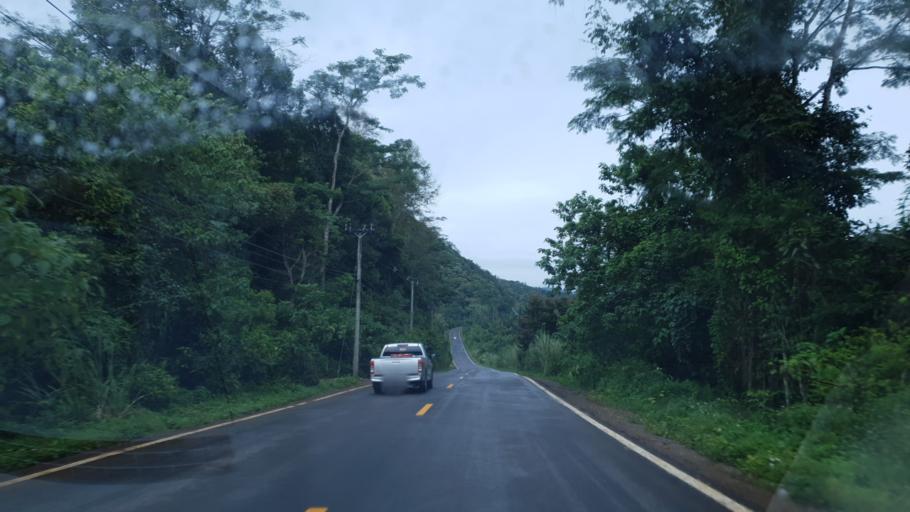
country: TH
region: Mae Hong Son
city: Ban Huai I Huak
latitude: 18.1477
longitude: 98.0991
